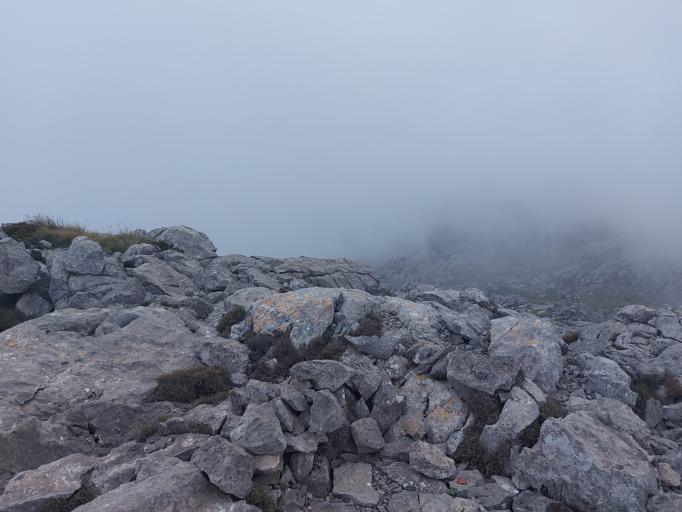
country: ES
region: Balearic Islands
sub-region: Illes Balears
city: Escorca
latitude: 39.8607
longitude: 2.8605
